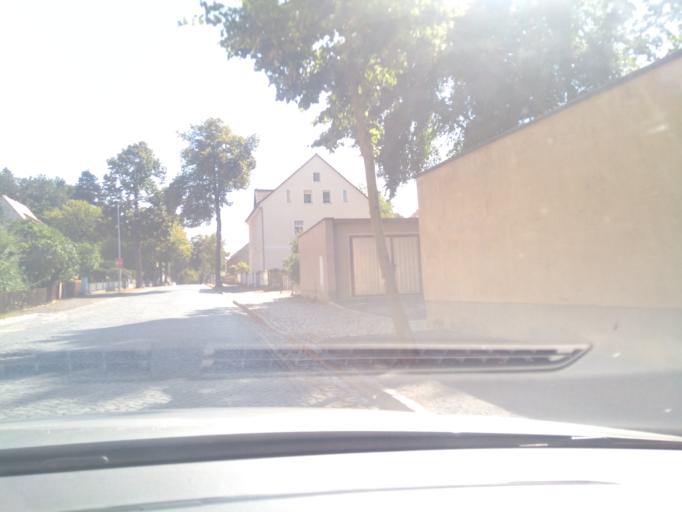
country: DE
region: Saxony
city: Kamenz
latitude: 51.2697
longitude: 14.1039
